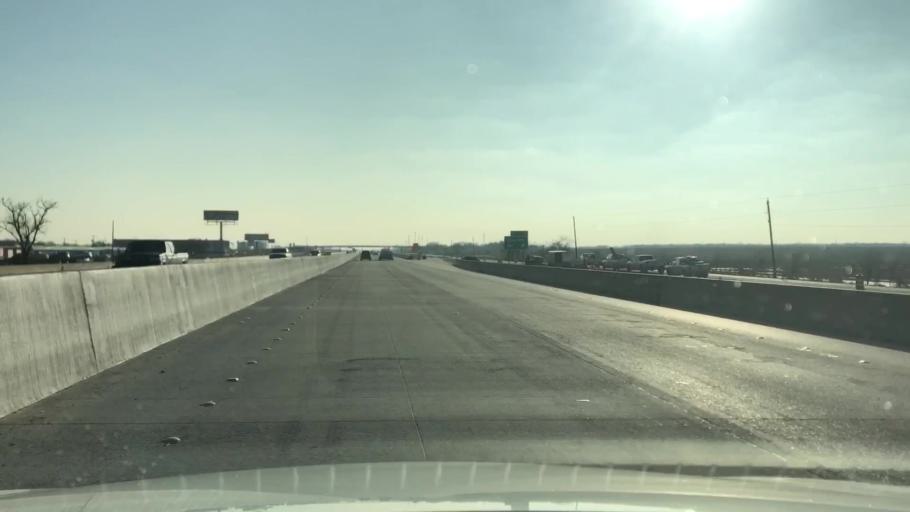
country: US
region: Texas
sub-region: Ellis County
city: Oak Leaf
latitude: 32.4808
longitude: -96.8325
